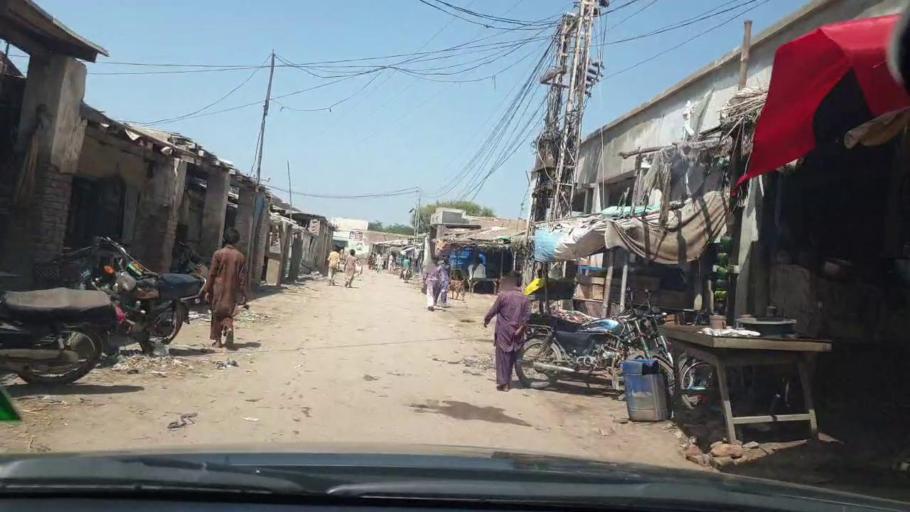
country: PK
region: Sindh
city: Tando Bago
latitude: 24.9256
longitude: 69.0573
